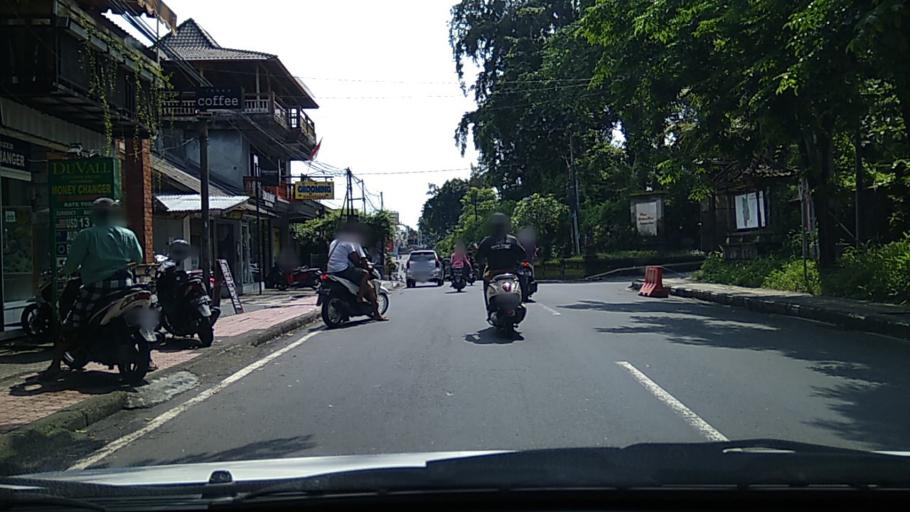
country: ID
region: Bali
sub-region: Kabupaten Gianyar
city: Ubud
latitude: -8.5090
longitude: 115.2688
